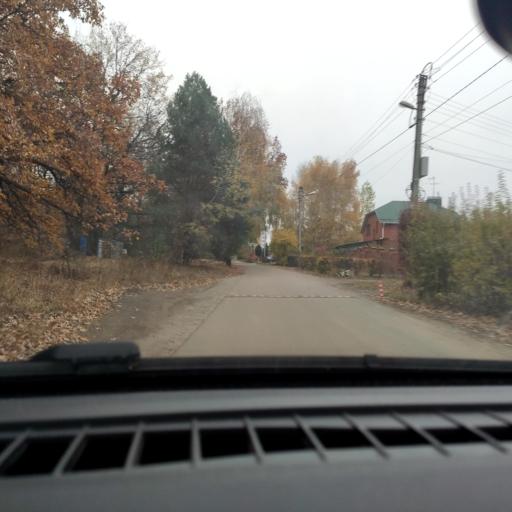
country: RU
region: Voronezj
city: Podgornoye
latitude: 51.7641
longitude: 39.1817
